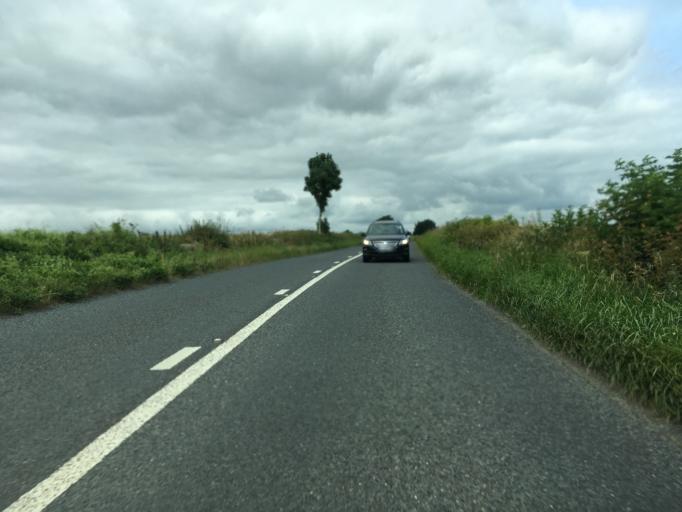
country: GB
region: England
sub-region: Gloucestershire
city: Bourton on the Water
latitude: 51.8860
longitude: -1.7894
